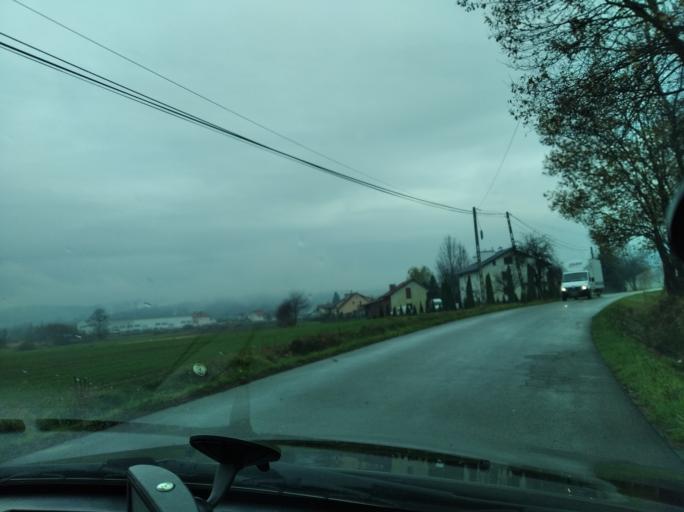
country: PL
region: Subcarpathian Voivodeship
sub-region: Powiat strzyzowski
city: Babica
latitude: 49.9274
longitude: 21.8560
